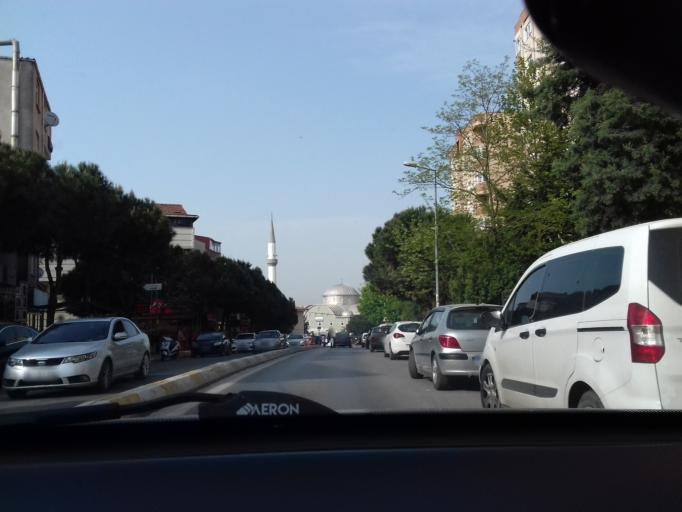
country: TR
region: Istanbul
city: Pendik
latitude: 40.9133
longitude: 29.2829
